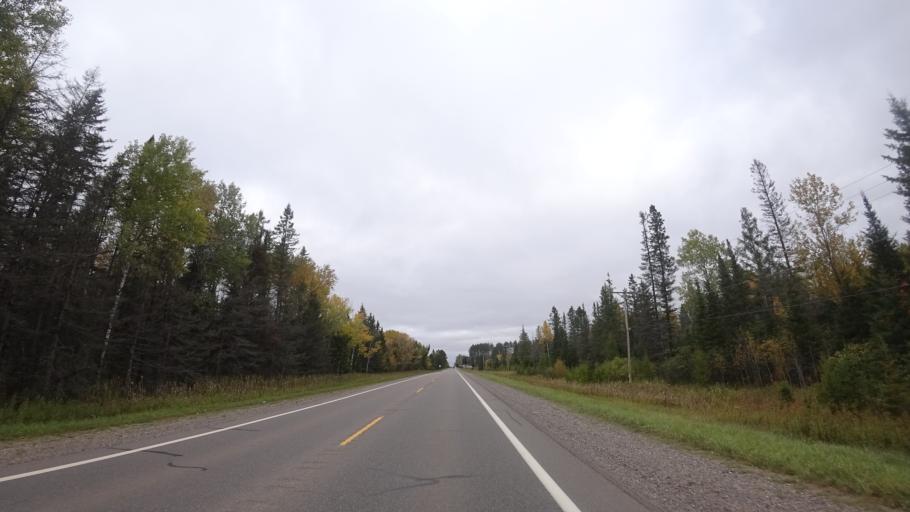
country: US
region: Michigan
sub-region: Iron County
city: Crystal Falls
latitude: 46.1310
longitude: -88.0922
